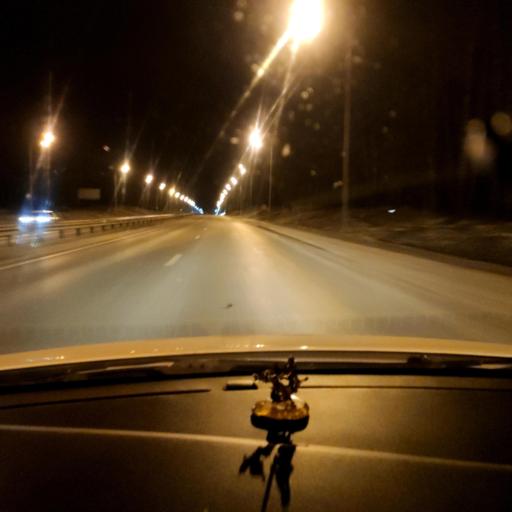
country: RU
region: Tatarstan
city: Osinovo
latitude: 55.8300
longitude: 48.8494
